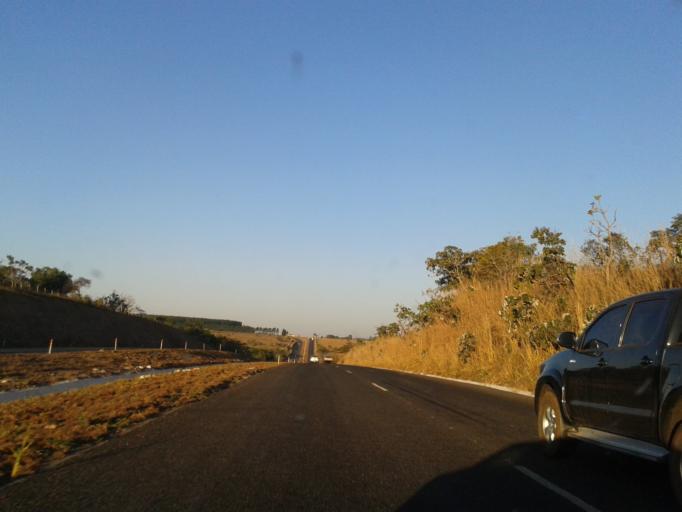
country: BR
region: Goias
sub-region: Goias
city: Goias
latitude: -16.0031
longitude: -50.0505
